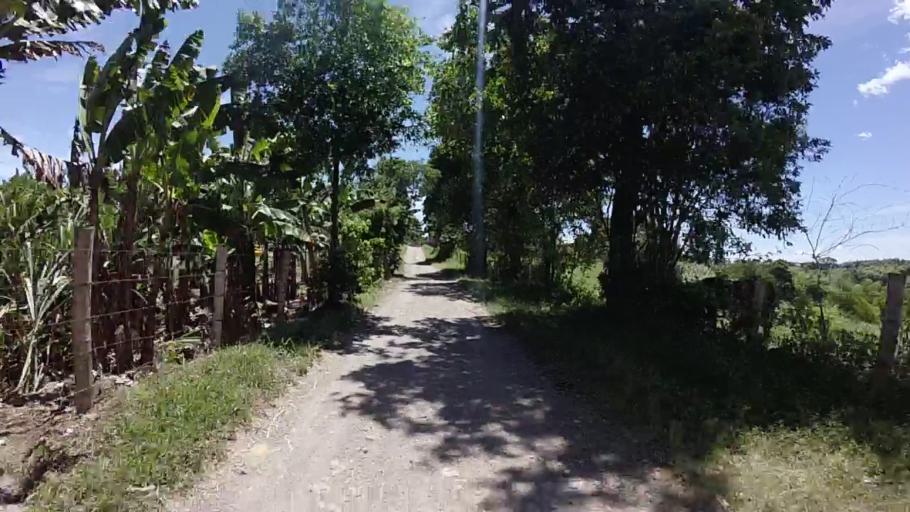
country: CO
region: Valle del Cauca
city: Ulloa
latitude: 4.7138
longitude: -75.7716
